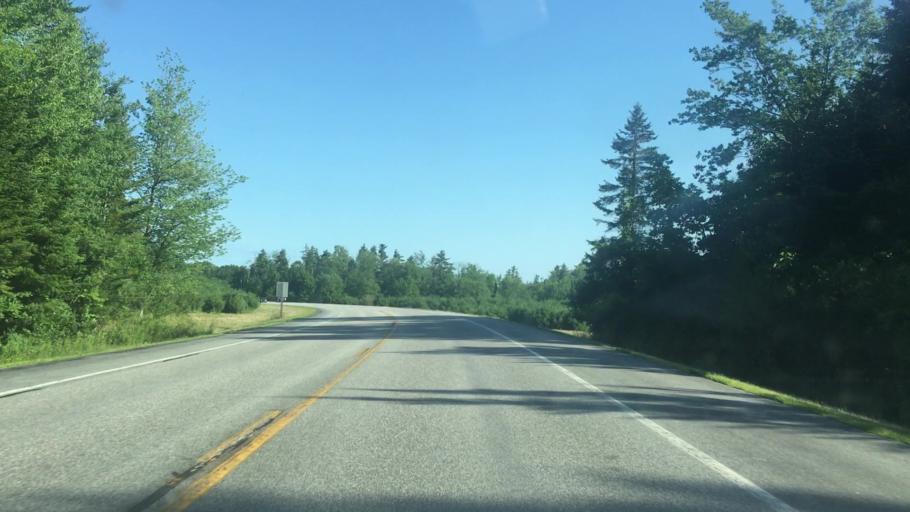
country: US
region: Maine
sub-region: Cumberland County
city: Gorham
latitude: 43.6534
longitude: -70.4482
